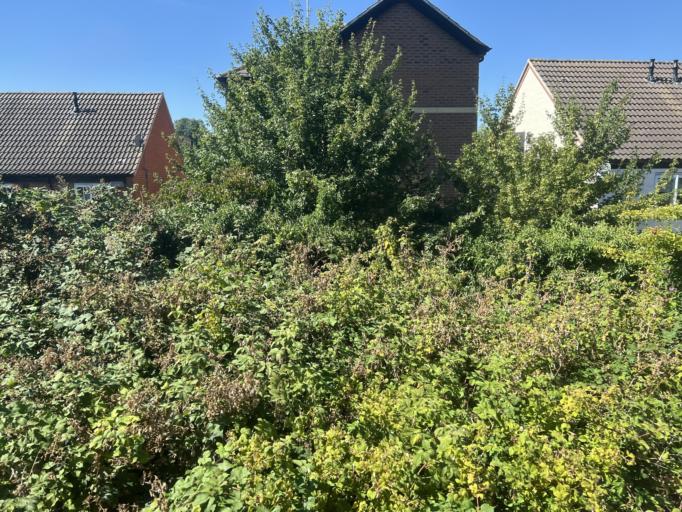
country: GB
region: England
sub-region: Lincolnshire
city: Boston
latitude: 52.9850
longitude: -0.0322
